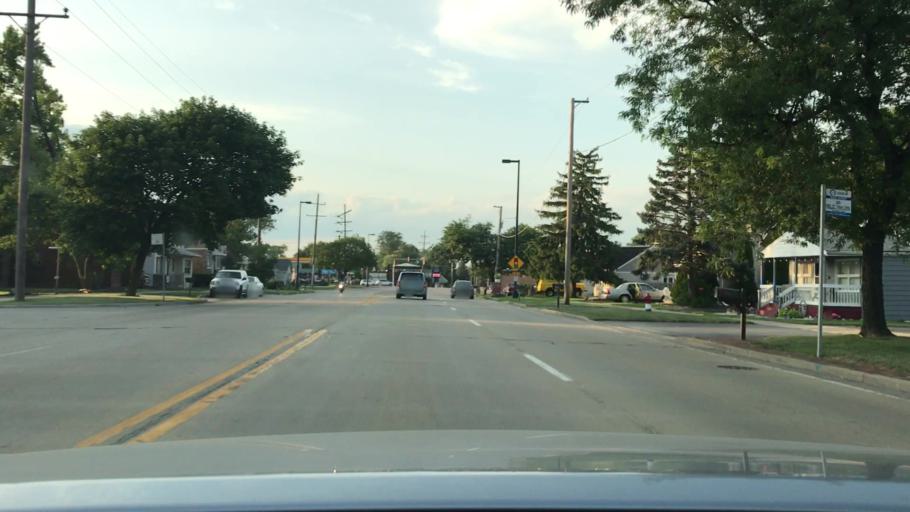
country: US
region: Illinois
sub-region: Cook County
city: Burbank
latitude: 41.7322
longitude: -87.7607
